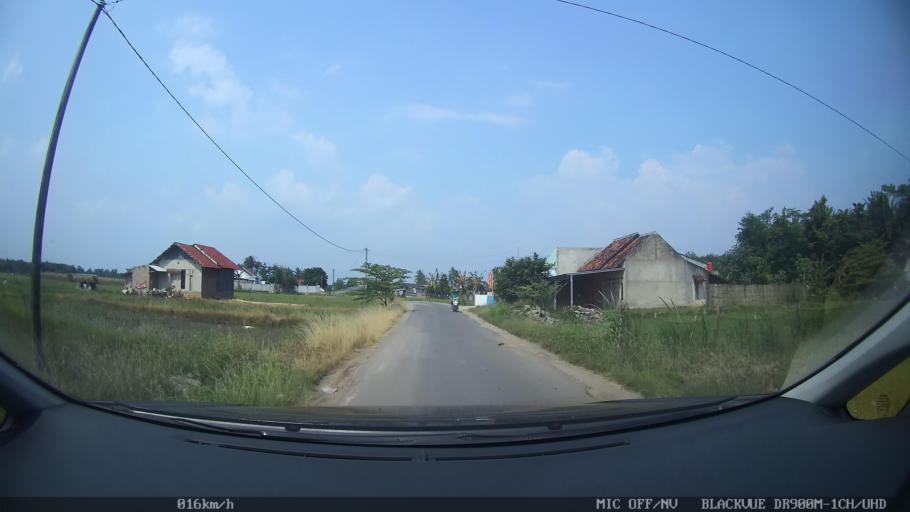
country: ID
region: Lampung
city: Natar
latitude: -5.3037
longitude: 105.2379
